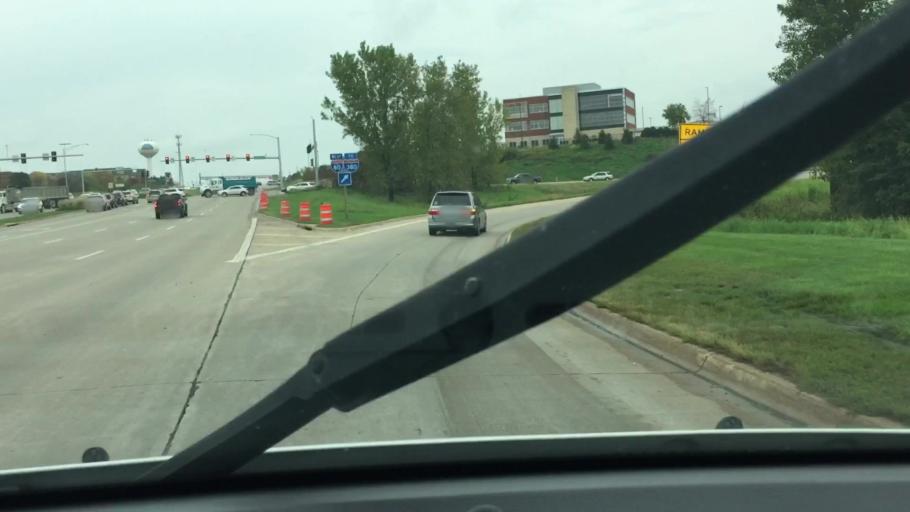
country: US
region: Iowa
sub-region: Johnson County
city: Coralville
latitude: 41.6946
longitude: -91.6082
